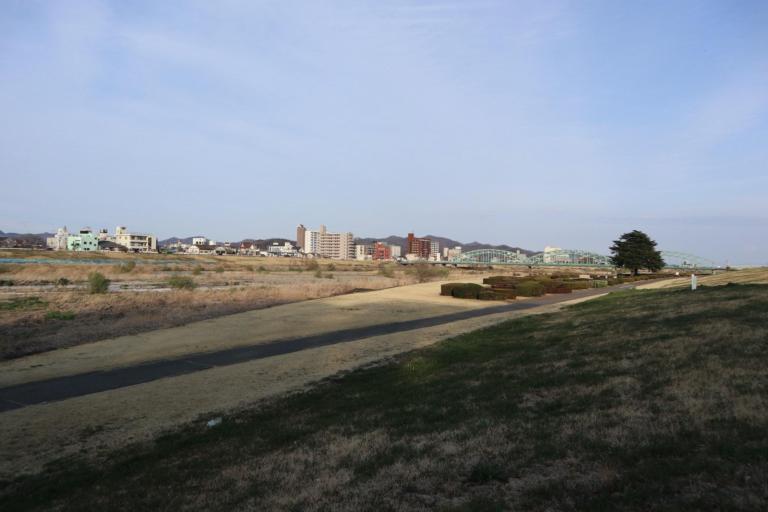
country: JP
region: Tochigi
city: Ashikaga
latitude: 36.3321
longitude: 139.4437
